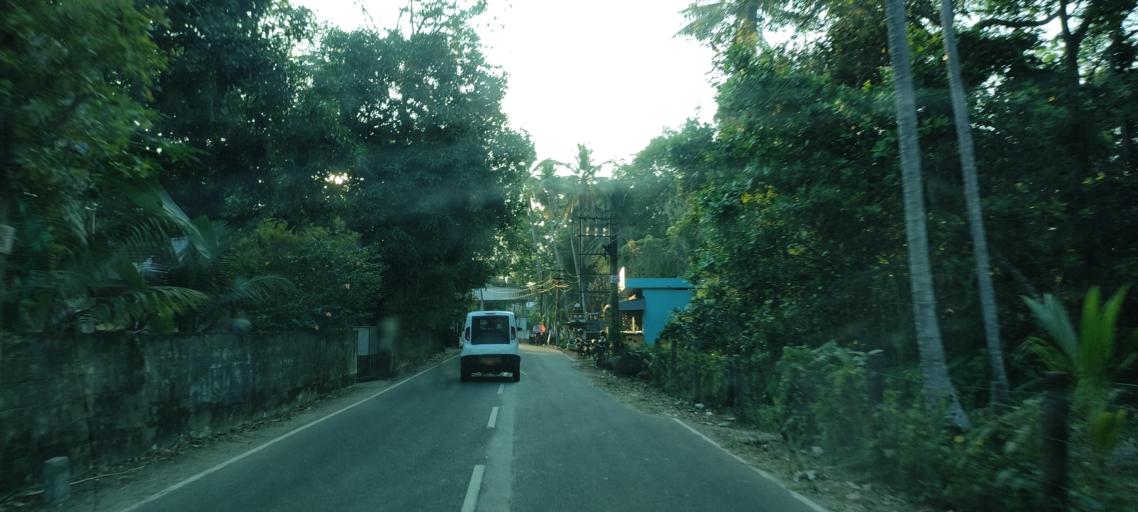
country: IN
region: Kerala
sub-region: Alappuzha
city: Kutiatodu
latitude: 9.7724
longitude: 76.3283
